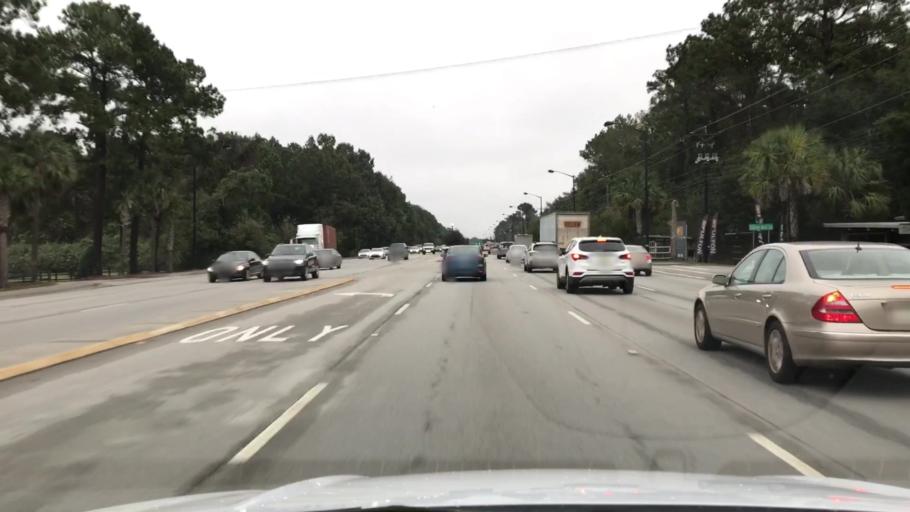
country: US
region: South Carolina
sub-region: Charleston County
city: Isle of Palms
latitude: 32.8485
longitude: -79.8091
